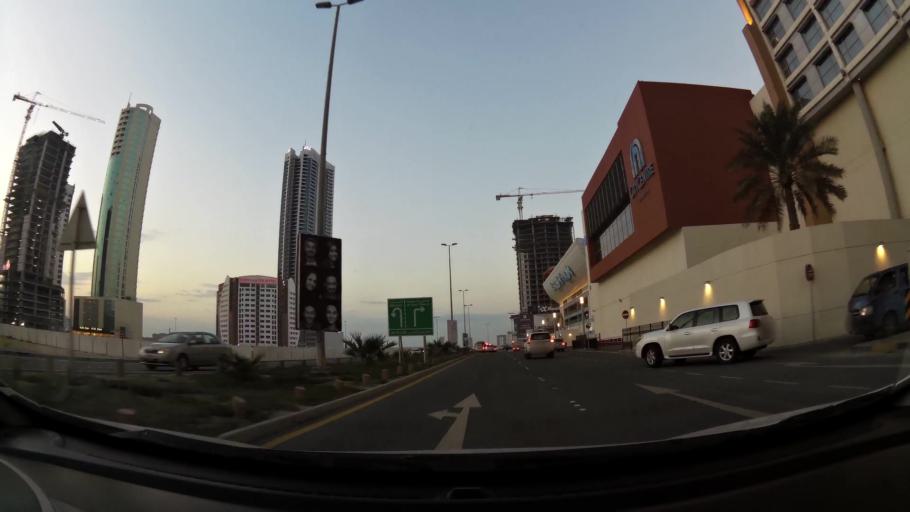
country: BH
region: Manama
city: Jidd Hafs
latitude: 26.2331
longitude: 50.5515
